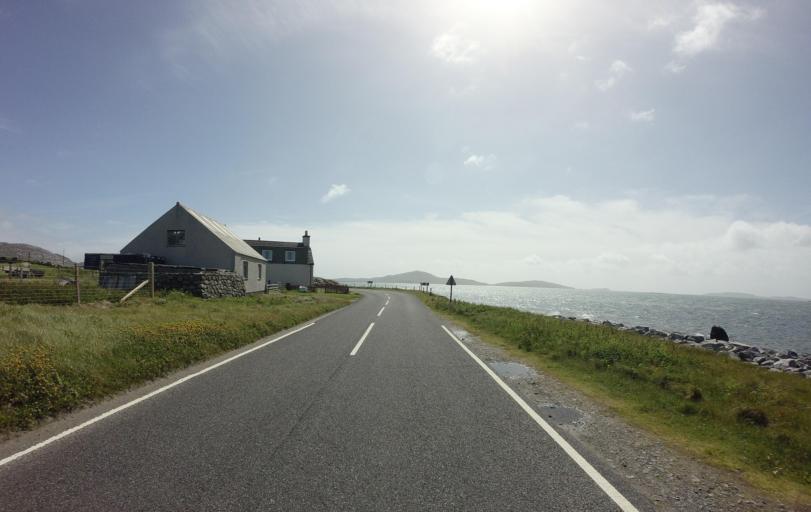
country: GB
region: Scotland
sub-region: Eilean Siar
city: Isle of South Uist
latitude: 57.1029
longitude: -7.3587
